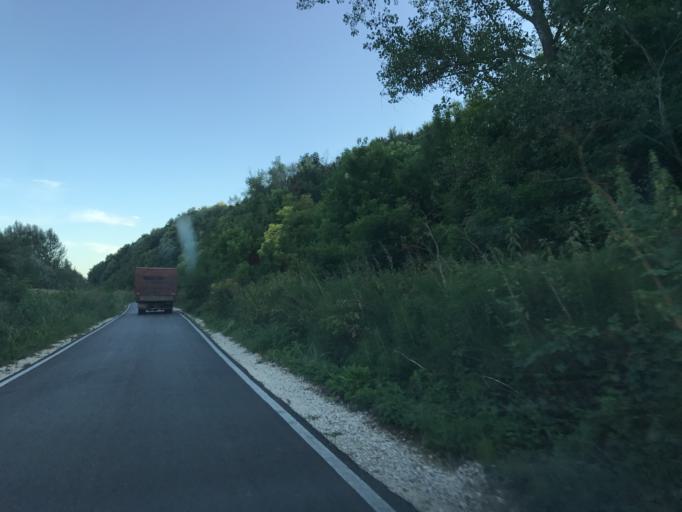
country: BG
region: Vidin
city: Bregovo
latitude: 44.1386
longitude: 22.6025
